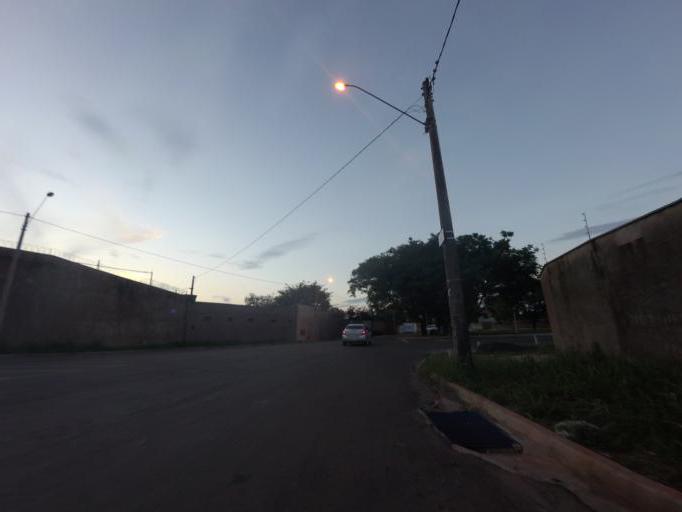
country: BR
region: Sao Paulo
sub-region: Piracicaba
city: Piracicaba
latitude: -22.7629
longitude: -47.5944
